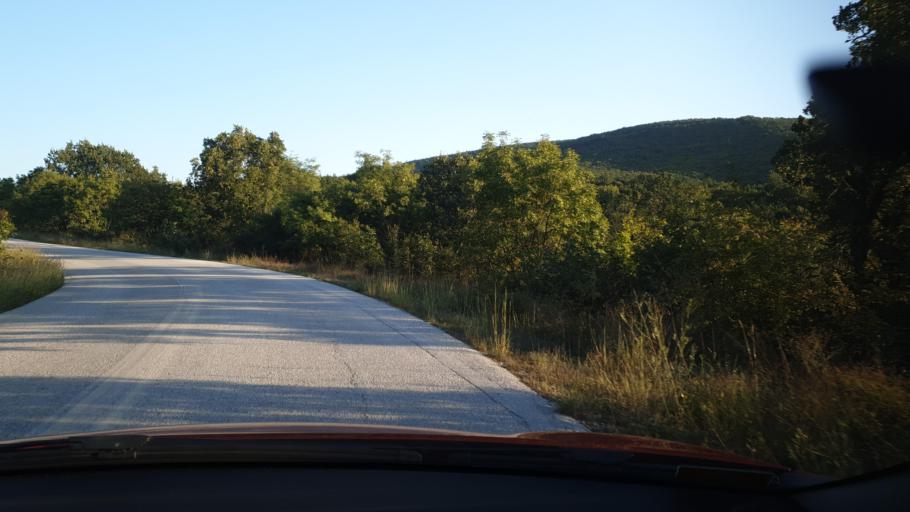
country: GR
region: Central Macedonia
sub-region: Nomos Chalkidikis
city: Galatista
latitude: 40.5490
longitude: 23.2822
